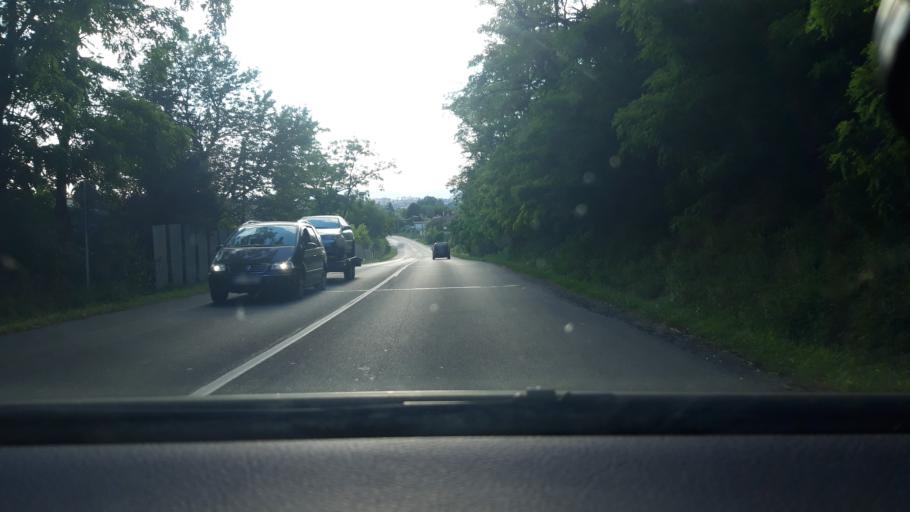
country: SK
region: Banskobystricky
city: Lucenec
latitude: 48.3271
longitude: 19.6935
